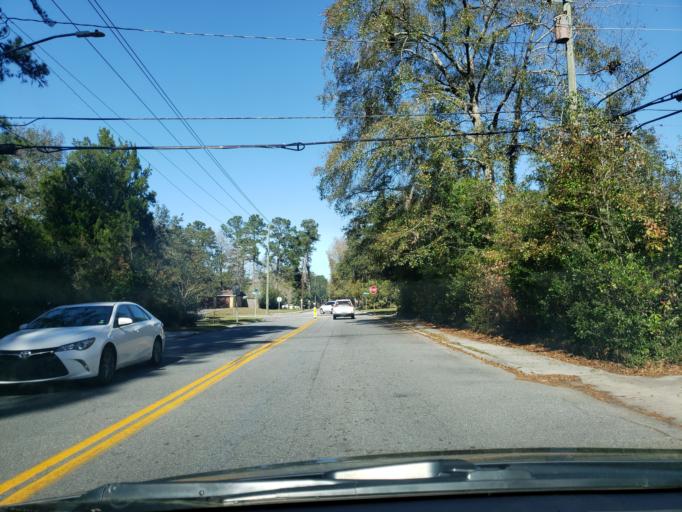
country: US
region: Georgia
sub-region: Chatham County
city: Montgomery
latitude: 31.9724
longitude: -81.1434
